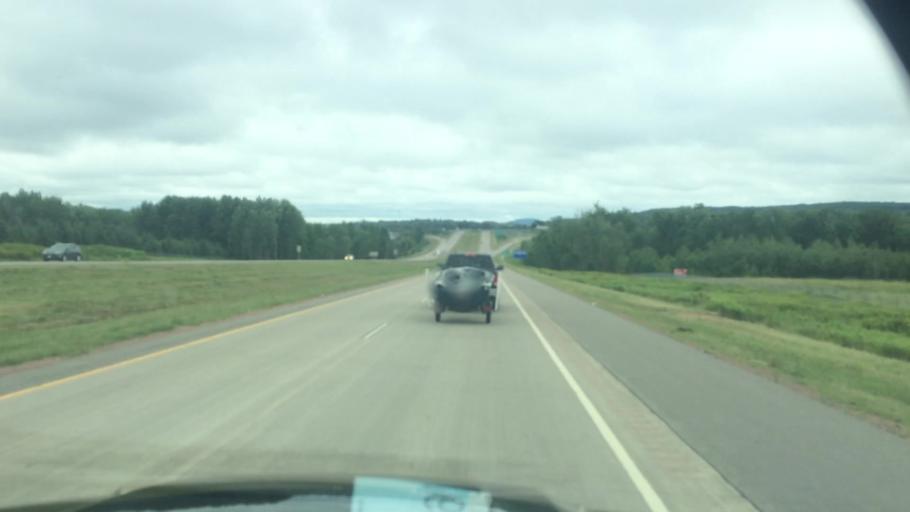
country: US
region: Wisconsin
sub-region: Marathon County
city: Wausau
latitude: 45.0018
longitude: -89.6585
